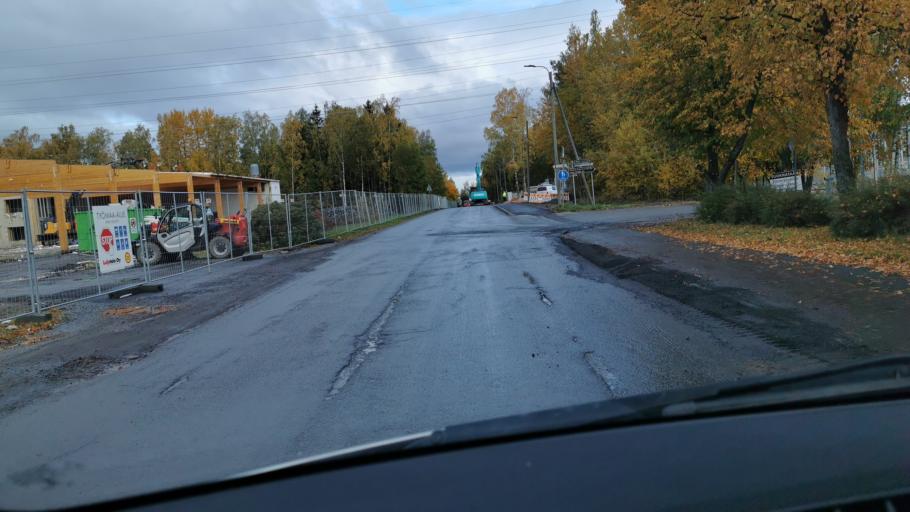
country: FI
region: Ostrobothnia
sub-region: Vaasa
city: Vaasa
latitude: 63.0905
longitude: 21.5639
